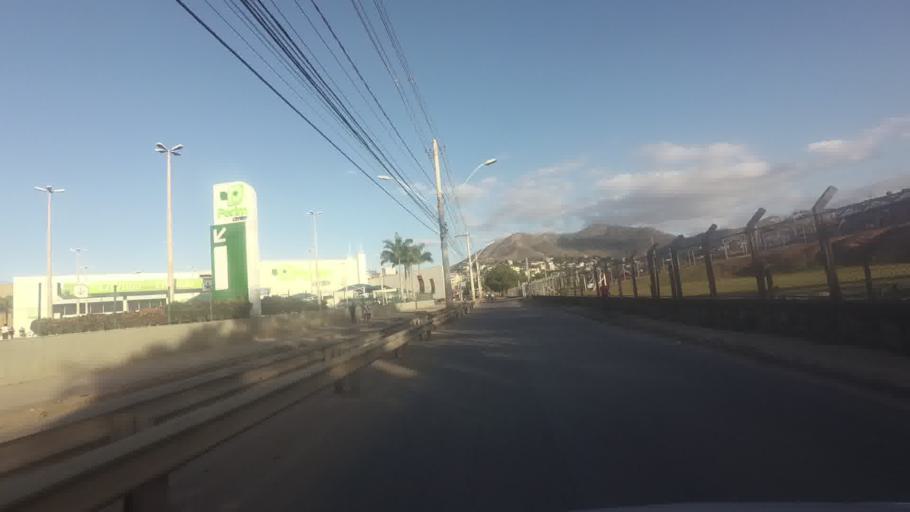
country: BR
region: Espirito Santo
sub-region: Cachoeiro De Itapemirim
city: Cachoeiro de Itapemirim
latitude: -20.8436
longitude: -41.1568
